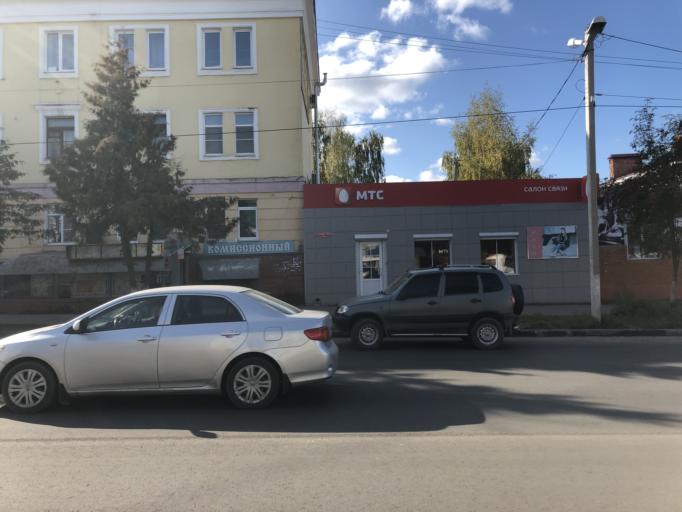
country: RU
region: Tverskaya
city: Rzhev
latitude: 56.2572
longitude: 34.3284
